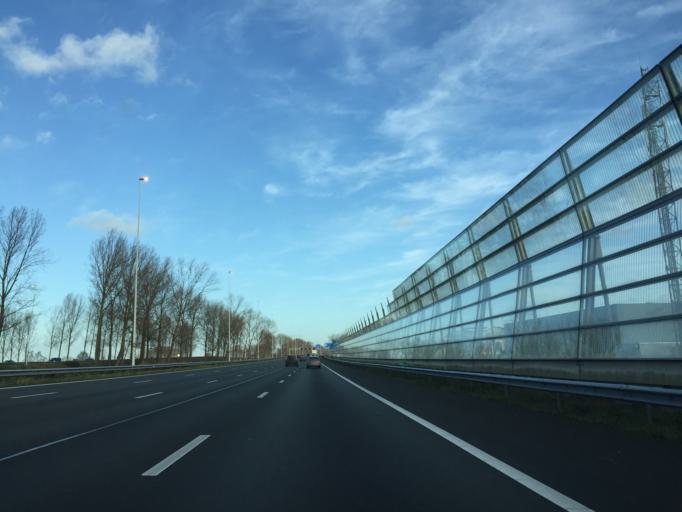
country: NL
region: South Holland
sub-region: Bodegraven-Reeuwijk
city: Reeuwijk
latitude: 52.0509
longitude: 4.7196
